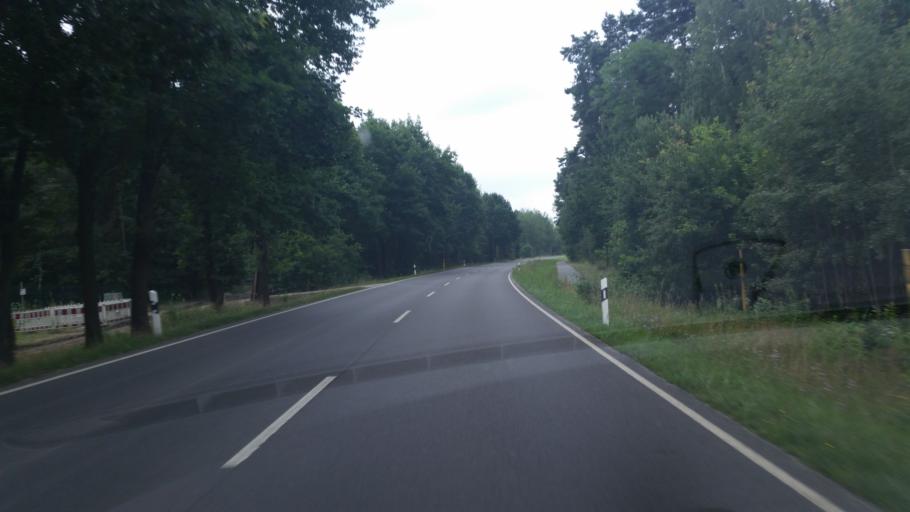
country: DE
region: Brandenburg
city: Senftenberg
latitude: 51.4815
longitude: 14.0698
